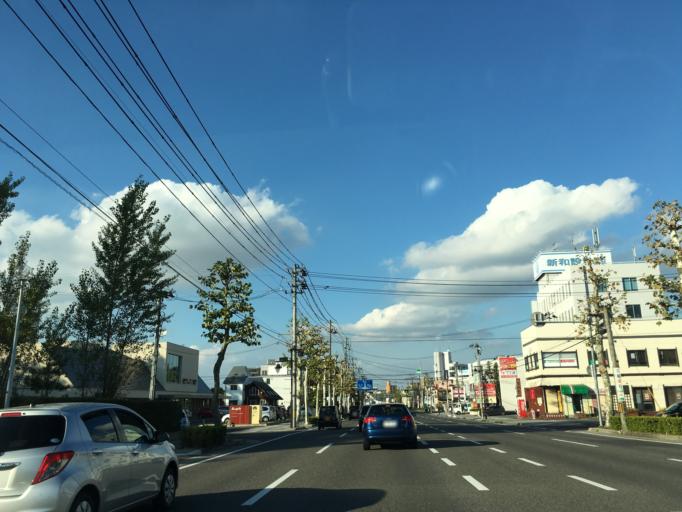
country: JP
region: Fukushima
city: Koriyama
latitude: 37.3975
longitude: 140.3629
